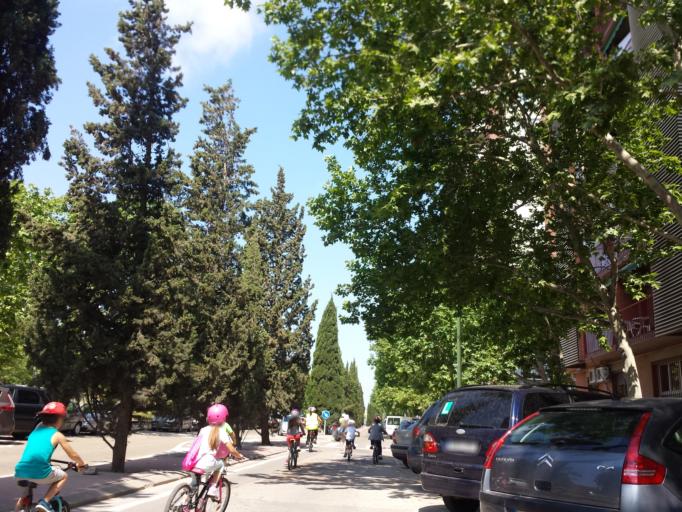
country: ES
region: Aragon
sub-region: Provincia de Zaragoza
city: Almozara
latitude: 41.6579
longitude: -0.8996
